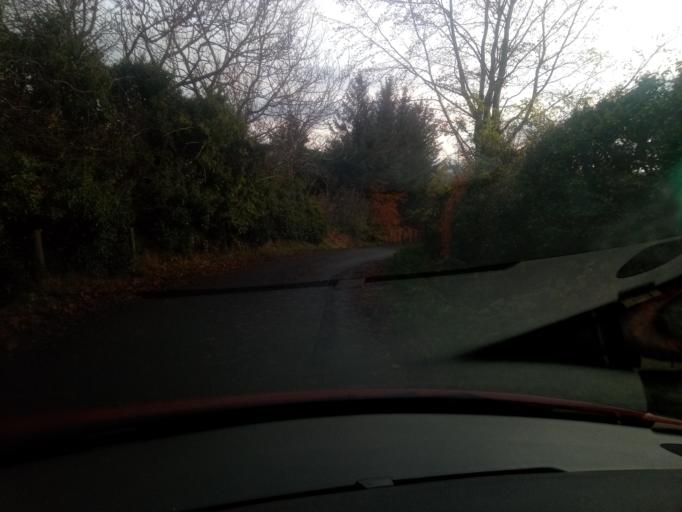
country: GB
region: Scotland
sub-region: The Scottish Borders
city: Jedburgh
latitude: 55.4790
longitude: -2.5616
